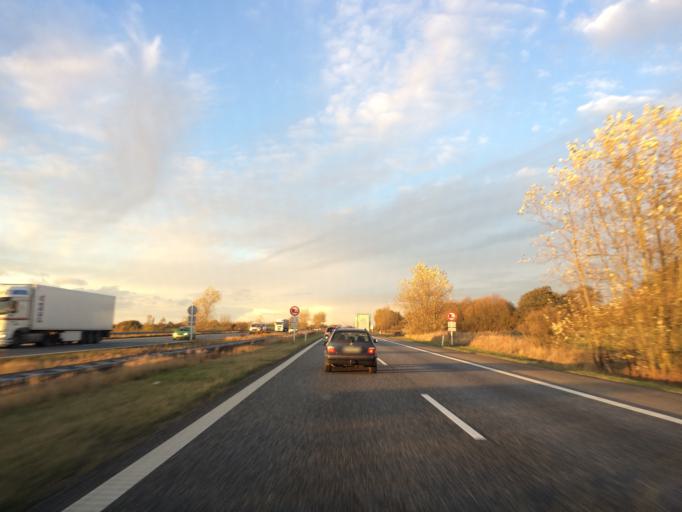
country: DK
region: South Denmark
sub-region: Kolding Kommune
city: Christiansfeld
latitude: 55.4103
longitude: 9.4552
